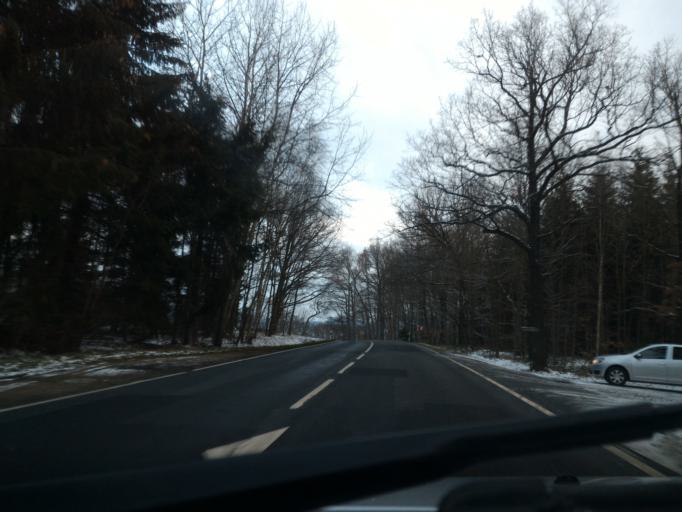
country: DE
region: Saxony
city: Leutersdorf
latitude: 50.9283
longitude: 14.6677
